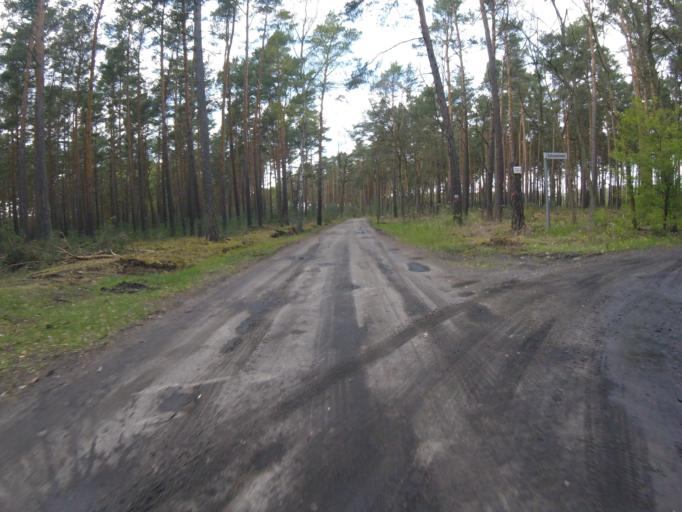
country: DE
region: Brandenburg
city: Munchehofe
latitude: 52.2168
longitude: 13.7695
